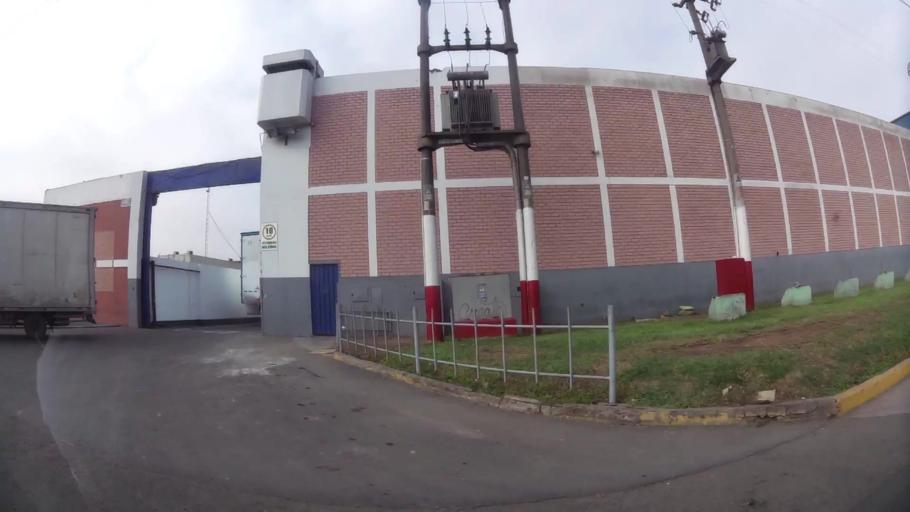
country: PE
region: Callao
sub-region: Callao
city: Callao
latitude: -12.0261
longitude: -77.1036
